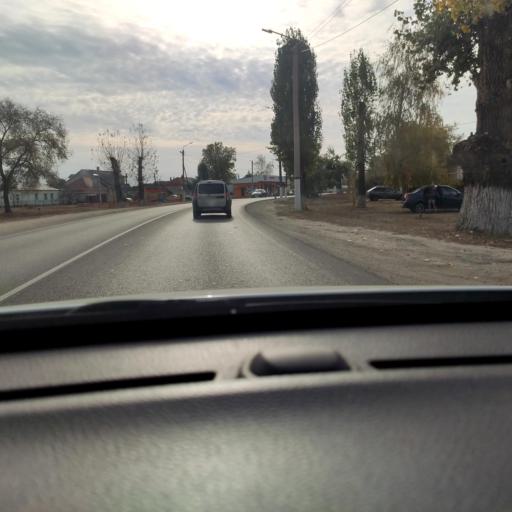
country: RU
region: Voronezj
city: Novaya Usman'
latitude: 51.6185
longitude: 39.3961
